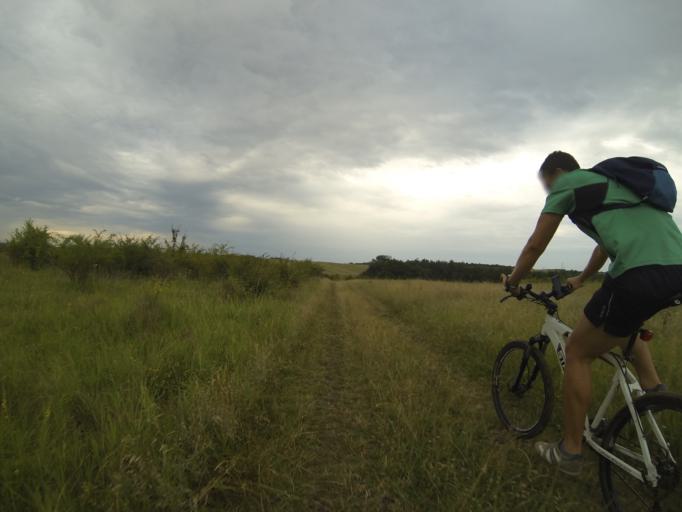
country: RO
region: Dolj
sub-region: Comuna Filiasi
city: Fratostita
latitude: 44.5710
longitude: 23.6212
